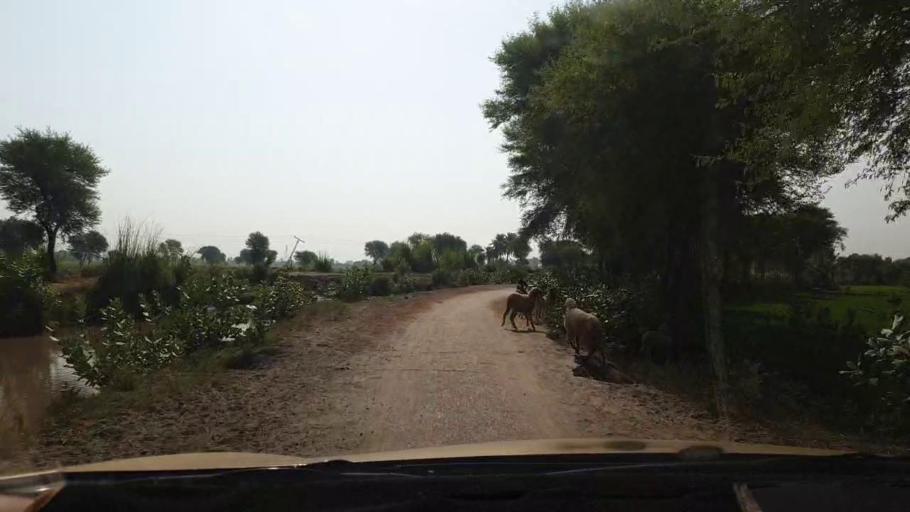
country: PK
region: Sindh
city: Larkana
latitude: 27.6259
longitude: 68.2588
